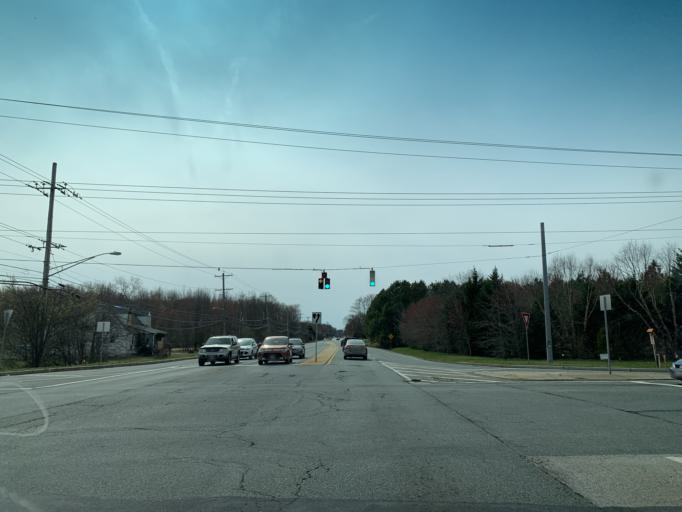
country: US
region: Delaware
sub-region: New Castle County
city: Glasgow
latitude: 39.6262
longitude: -75.7728
